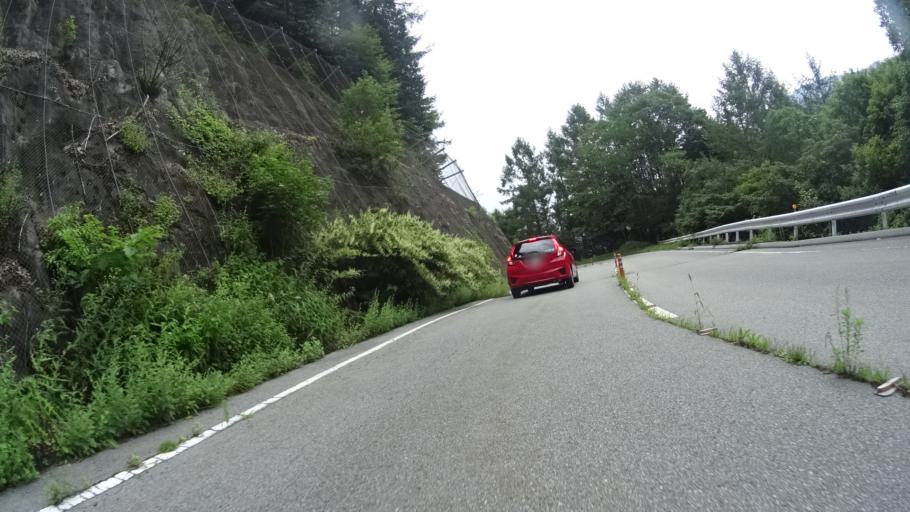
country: JP
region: Yamanashi
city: Enzan
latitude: 35.7984
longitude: 138.6759
